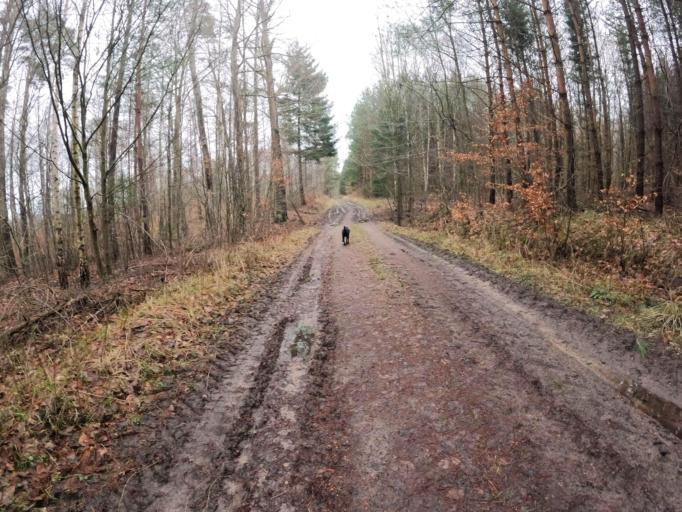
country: PL
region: West Pomeranian Voivodeship
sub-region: Powiat slawienski
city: Darlowo
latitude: 54.3967
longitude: 16.4698
